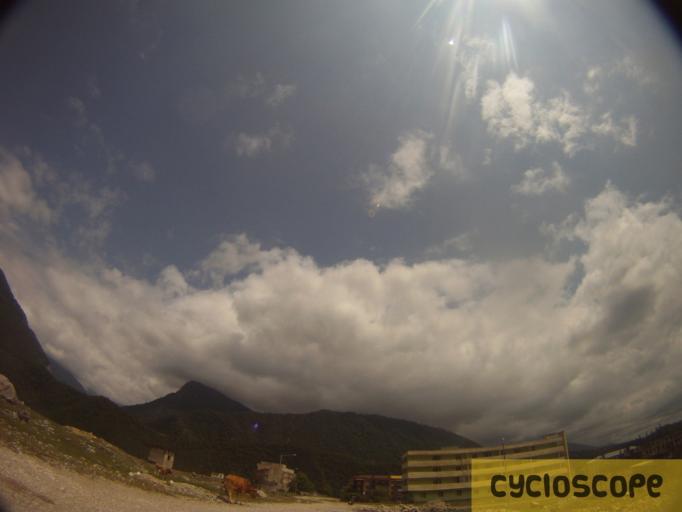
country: GE
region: Samegrelo and Zemo Svaneti
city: Jvari
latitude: 42.7486
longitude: 42.0389
